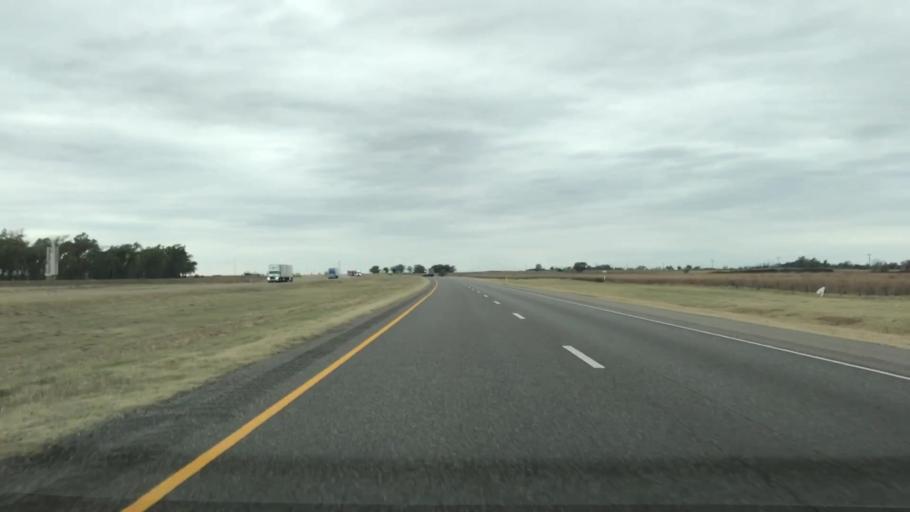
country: US
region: Oklahoma
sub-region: Beckham County
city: Erick
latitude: 35.2318
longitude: -99.9489
